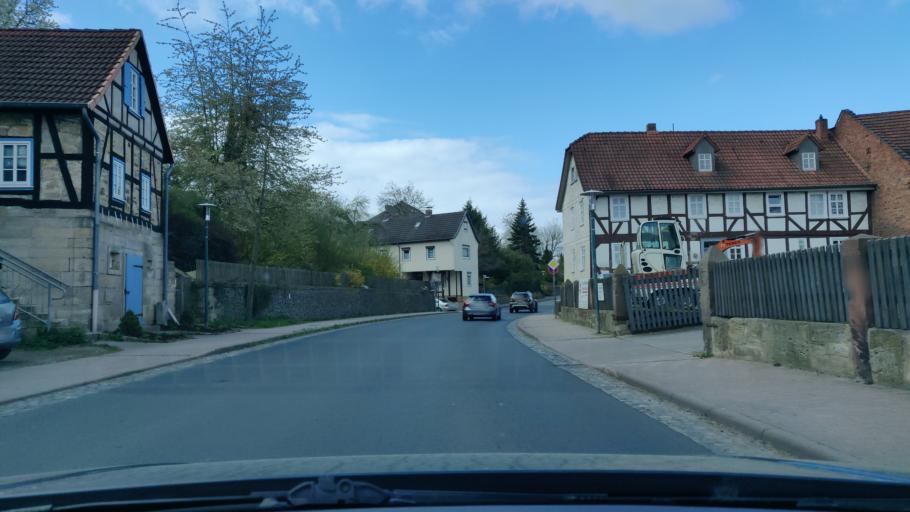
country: DE
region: Hesse
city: Felsberg
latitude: 51.1277
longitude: 9.4369
